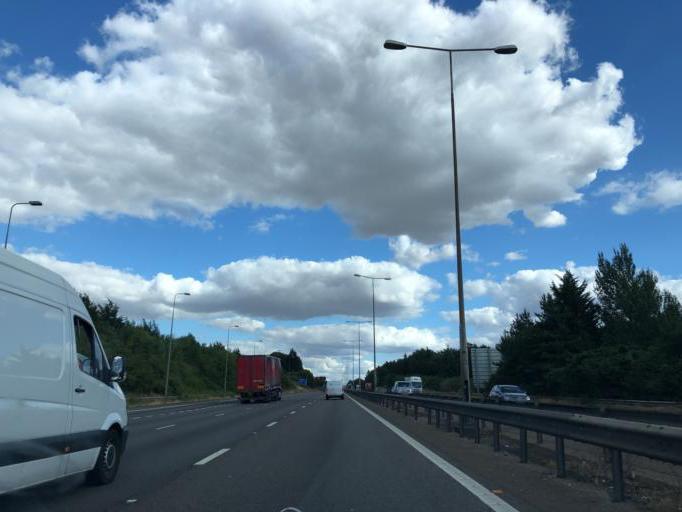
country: GB
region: England
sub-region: Northamptonshire
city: Roade
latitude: 52.1820
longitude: -0.8884
